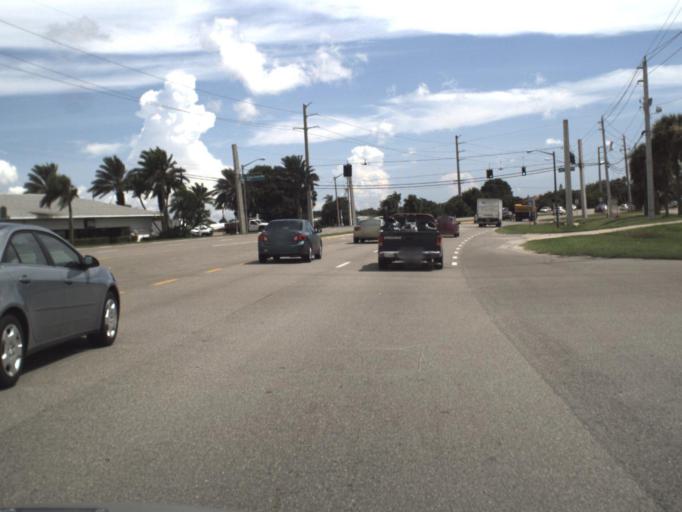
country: US
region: Florida
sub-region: Sarasota County
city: Nokomis
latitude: 27.1049
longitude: -82.4349
